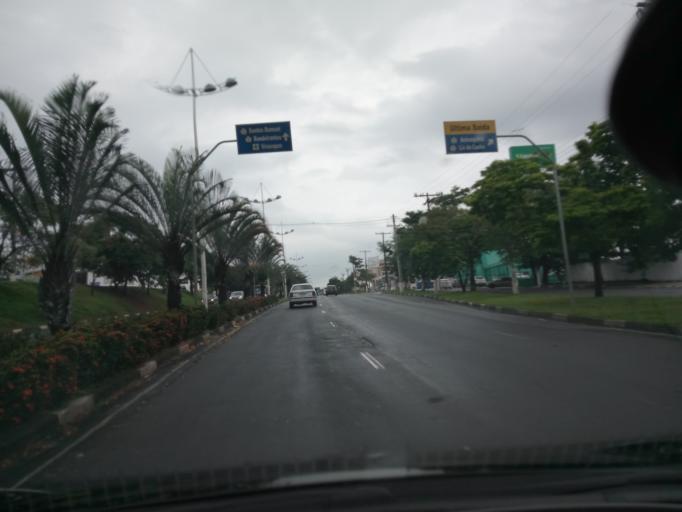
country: BR
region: Sao Paulo
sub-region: Campinas
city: Campinas
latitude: -22.9268
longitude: -47.0681
